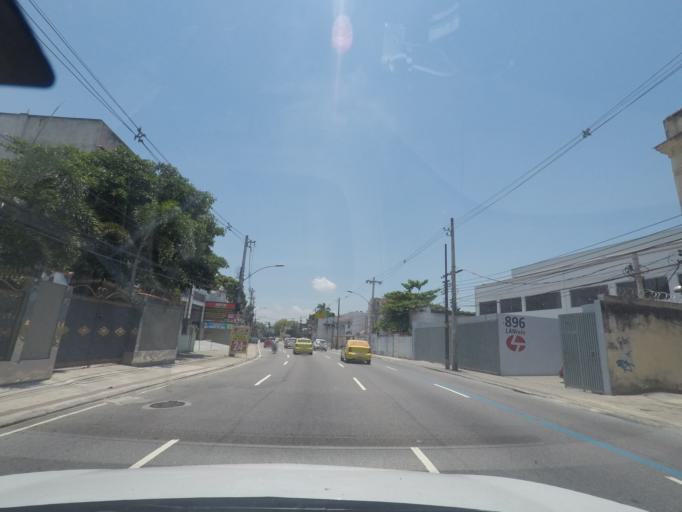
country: BR
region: Rio de Janeiro
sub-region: Rio De Janeiro
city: Rio de Janeiro
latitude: -22.9037
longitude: -43.2439
